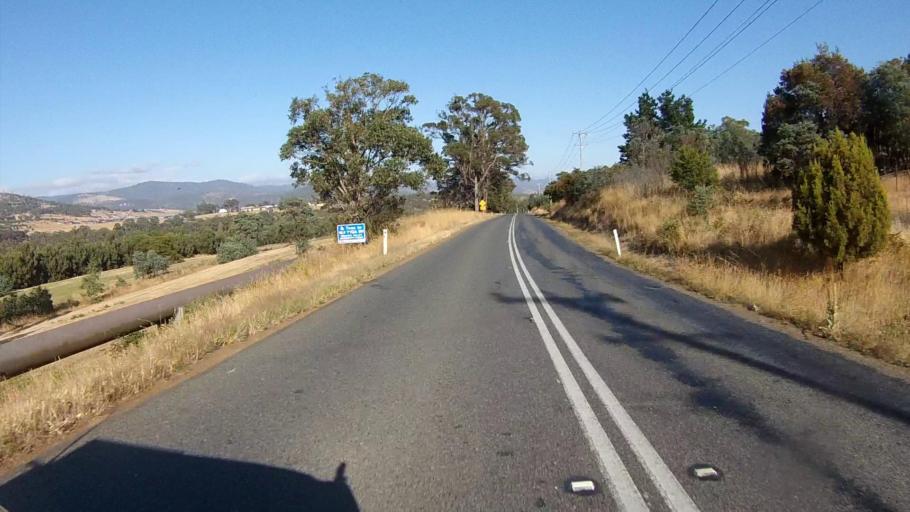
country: AU
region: Tasmania
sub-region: Derwent Valley
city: New Norfolk
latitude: -42.7779
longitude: 147.0933
